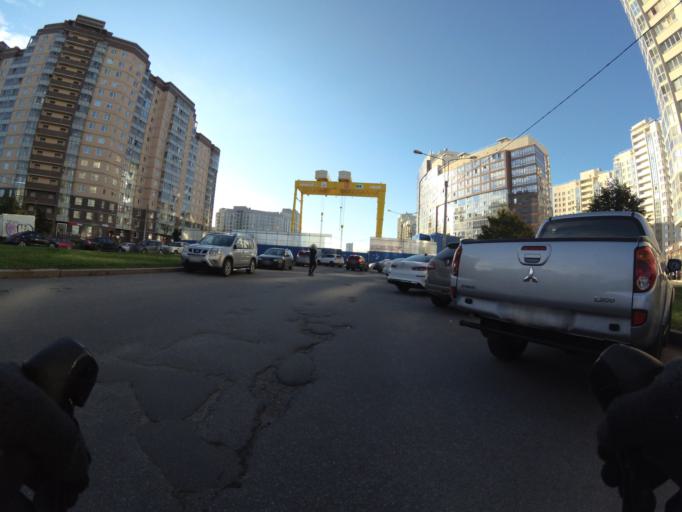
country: RU
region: Leningrad
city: Untolovo
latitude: 60.0003
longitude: 30.2085
